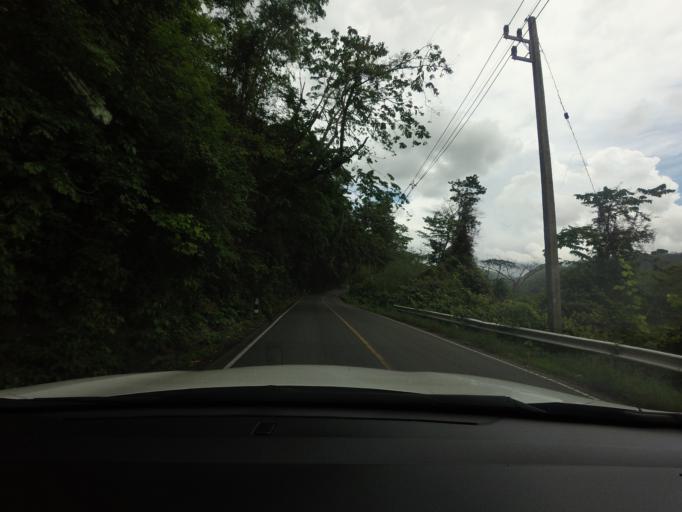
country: TH
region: Nakhon Ratchasima
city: Pak Chong
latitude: 14.4910
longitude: 101.3865
